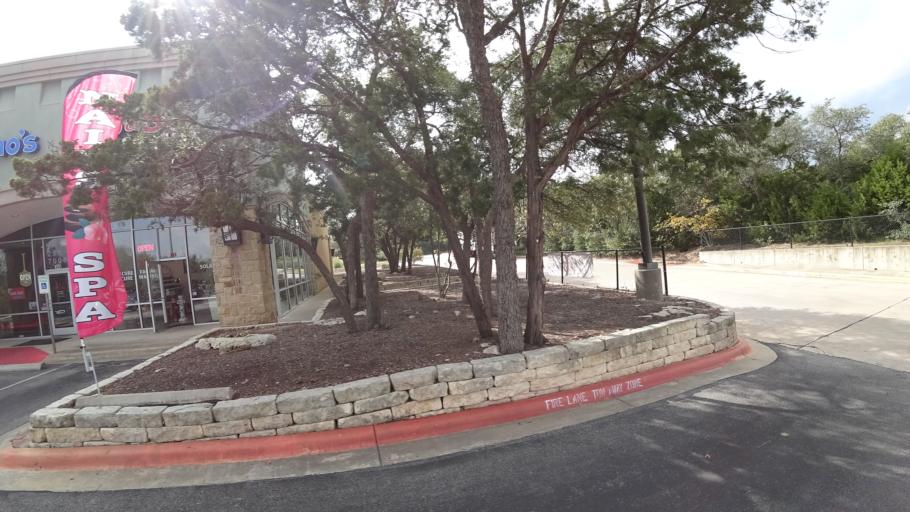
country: US
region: Texas
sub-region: Williamson County
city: Anderson Mill
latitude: 30.4135
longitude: -97.8505
